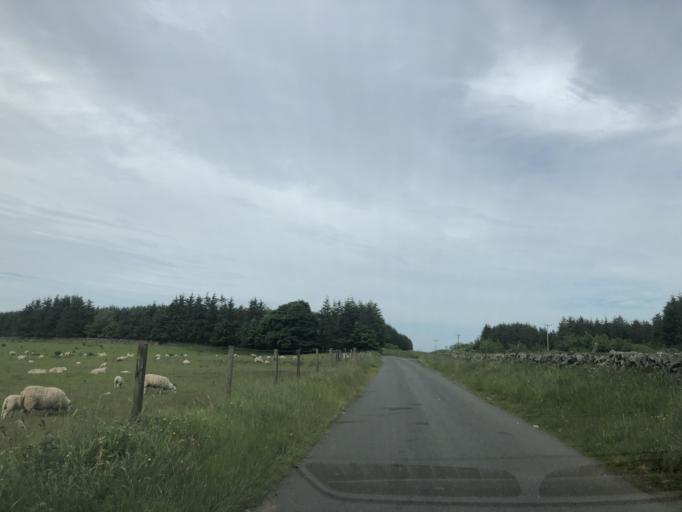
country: GB
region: Scotland
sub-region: The Scottish Borders
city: West Linton
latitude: 55.7698
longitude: -3.3195
